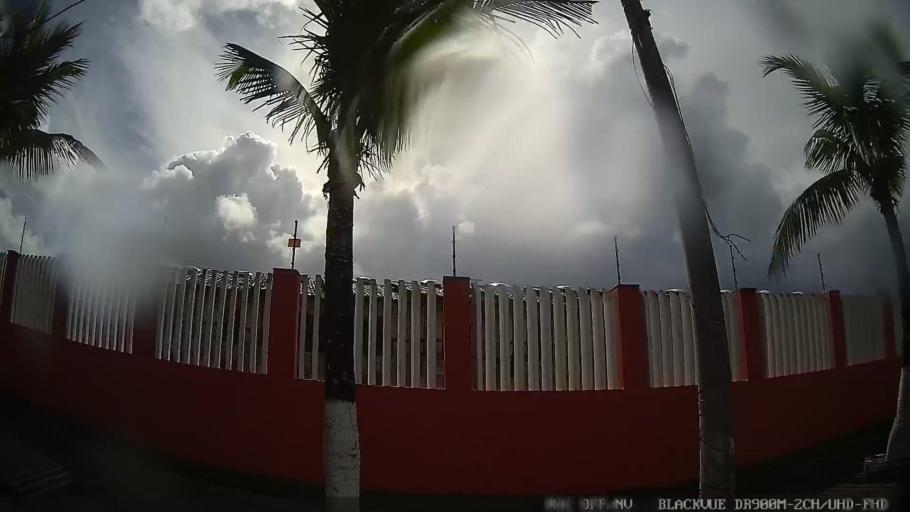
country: BR
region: Sao Paulo
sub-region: Itanhaem
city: Itanhaem
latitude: -24.2388
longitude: -46.8733
